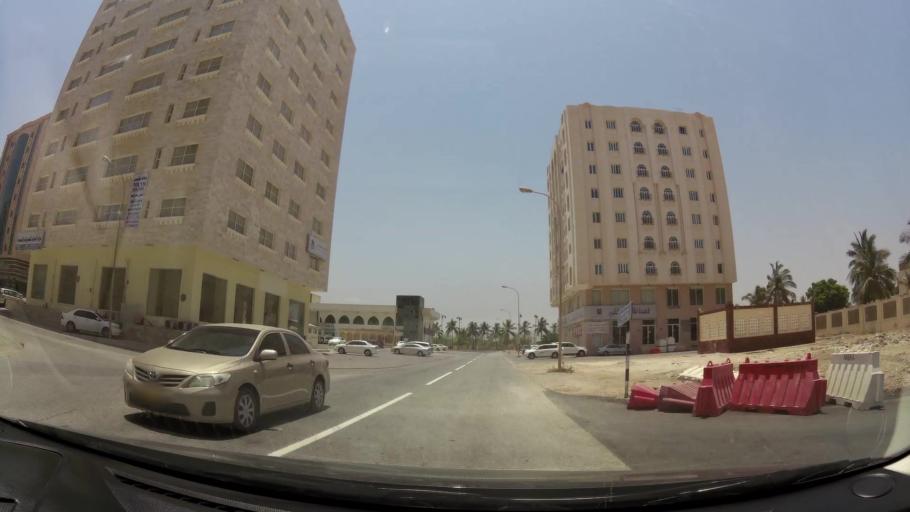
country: OM
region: Zufar
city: Salalah
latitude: 17.0224
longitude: 54.0936
